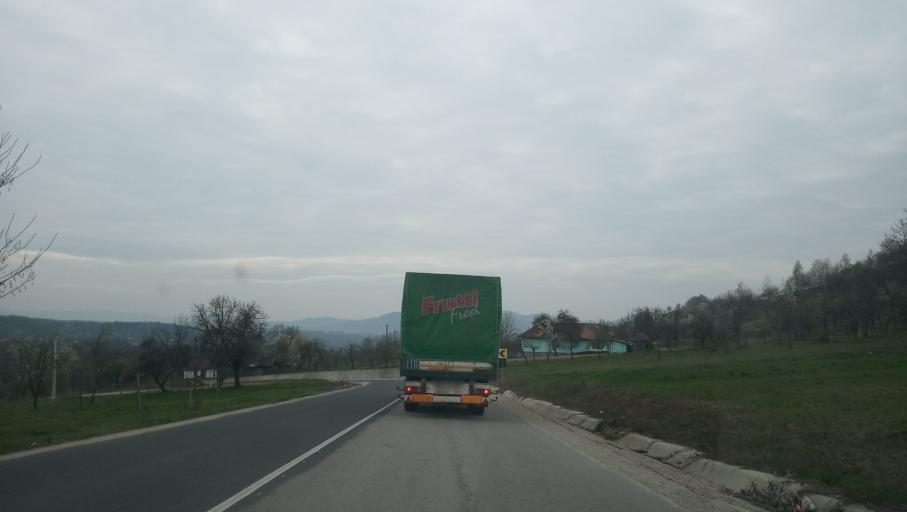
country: RO
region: Arad
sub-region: Comuna Varfurile
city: Varfurile
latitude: 46.3438
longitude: 22.5539
